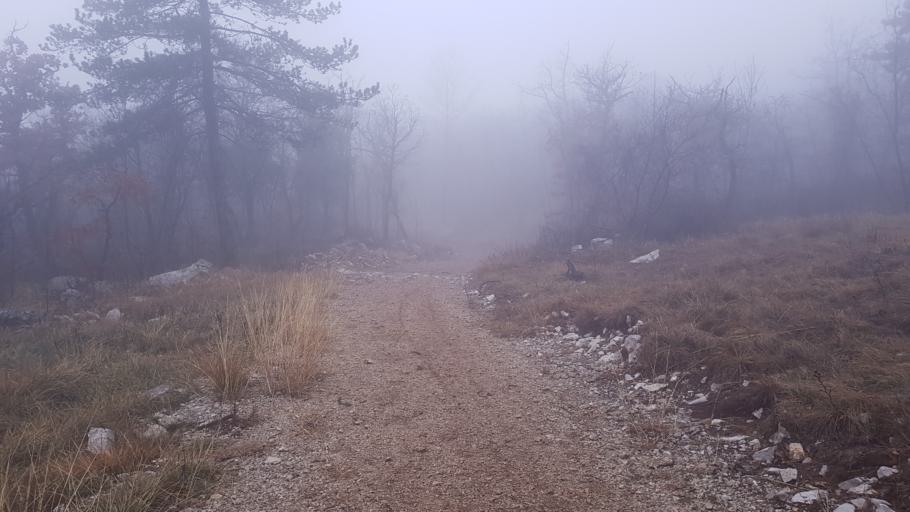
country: IT
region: Friuli Venezia Giulia
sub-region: Provincia di Trieste
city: Zolla
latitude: 45.7156
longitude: 13.8210
